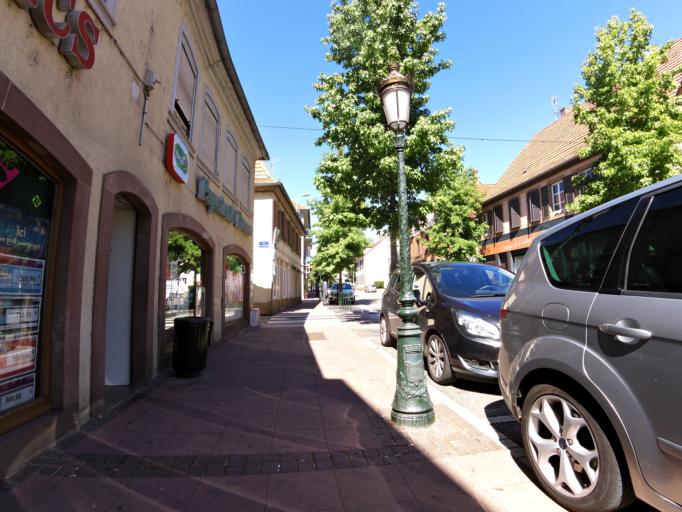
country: FR
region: Alsace
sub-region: Departement du Bas-Rhin
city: Haguenau
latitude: 48.8189
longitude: 7.7911
